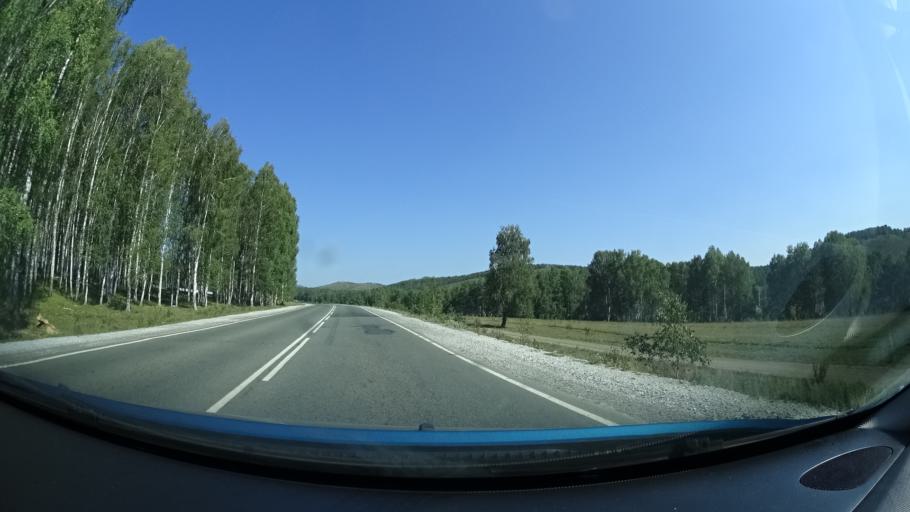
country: RU
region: Bashkortostan
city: Abzakovo
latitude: 53.8444
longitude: 58.5825
